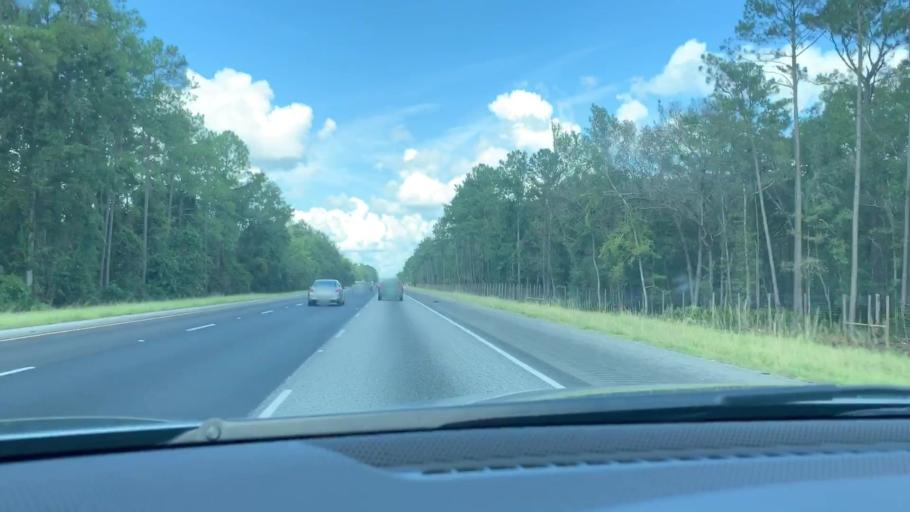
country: US
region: Georgia
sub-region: Camden County
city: Woodbine
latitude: 30.9073
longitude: -81.6858
